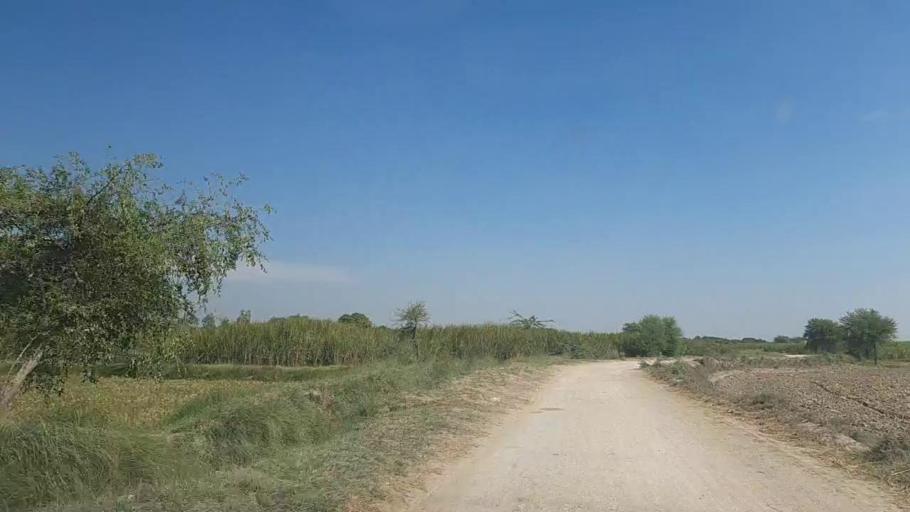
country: PK
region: Sindh
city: Mirpur Batoro
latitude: 24.7510
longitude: 68.2833
